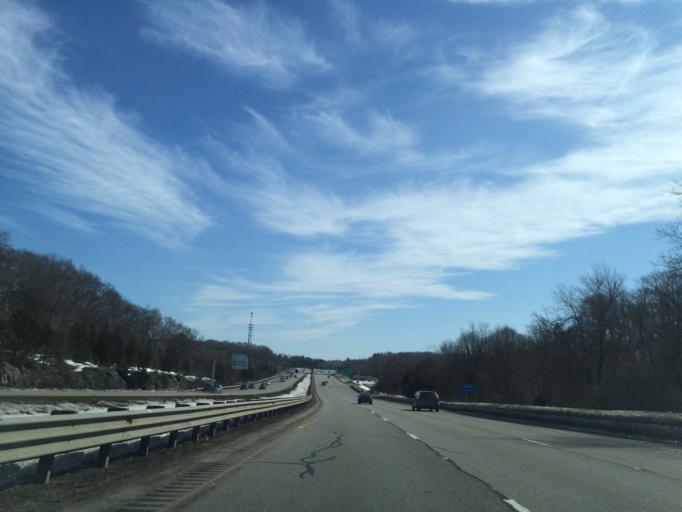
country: US
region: Massachusetts
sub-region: Middlesex County
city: Lexington
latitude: 42.4177
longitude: -71.2121
